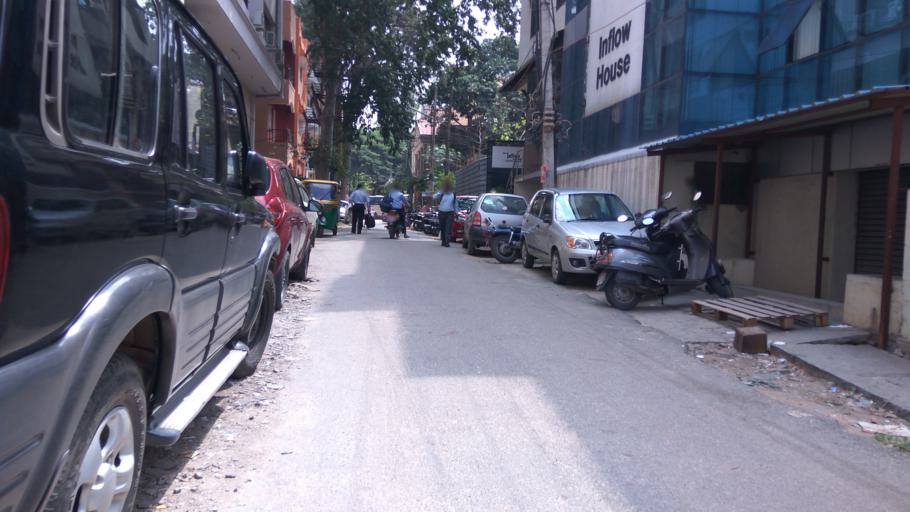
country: IN
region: Karnataka
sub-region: Bangalore Urban
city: Bangalore
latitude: 12.9780
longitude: 77.6399
